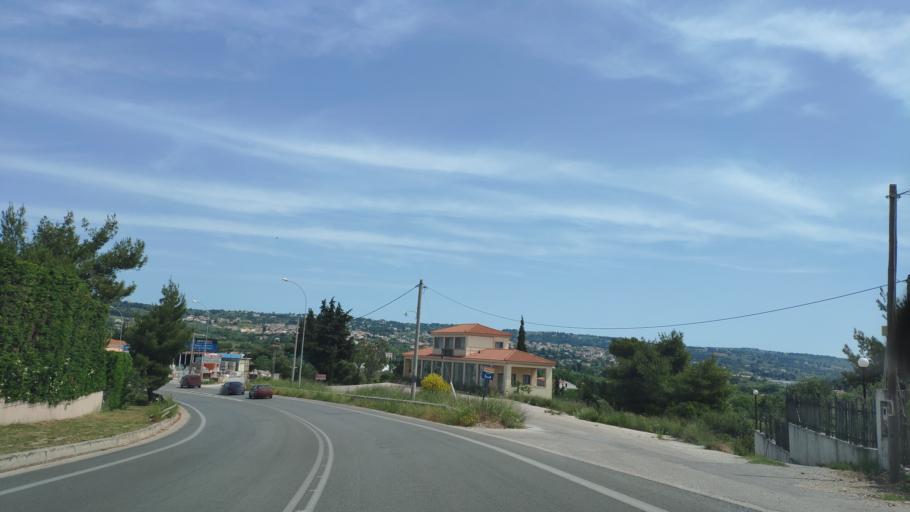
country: GR
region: Attica
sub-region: Nomarchia Anatolikis Attikis
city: Afidnes
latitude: 38.2003
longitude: 23.8571
